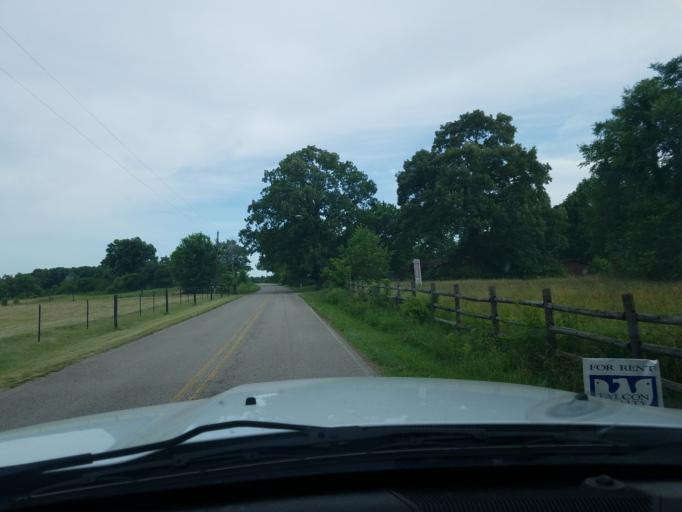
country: US
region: Tennessee
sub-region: Putnam County
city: Baxter
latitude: 36.1292
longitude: -85.5815
